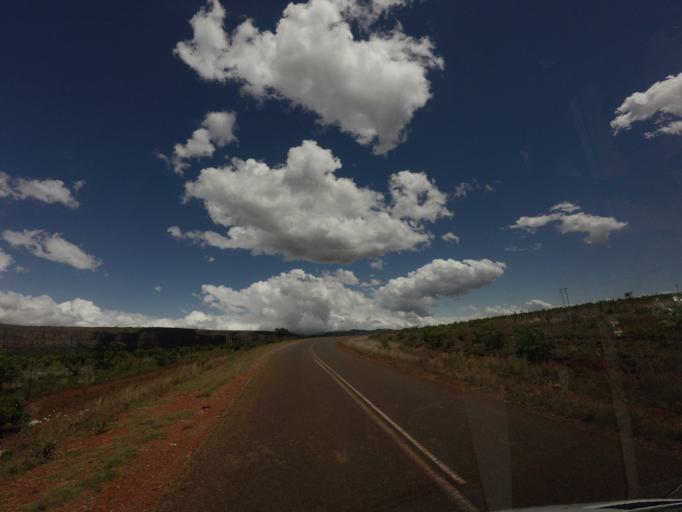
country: ZA
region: Limpopo
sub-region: Mopani District Municipality
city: Hoedspruit
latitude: -24.6167
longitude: 30.8188
